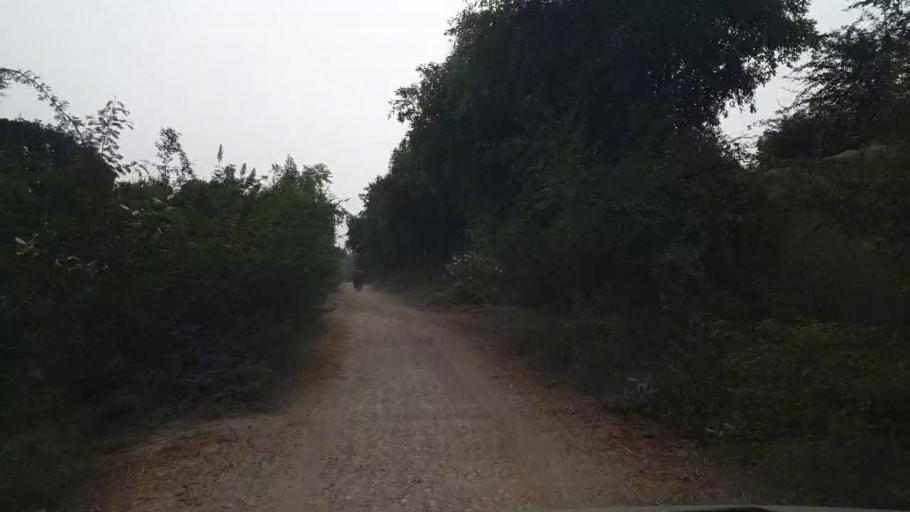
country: PK
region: Sindh
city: Matli
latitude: 24.9892
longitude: 68.7025
